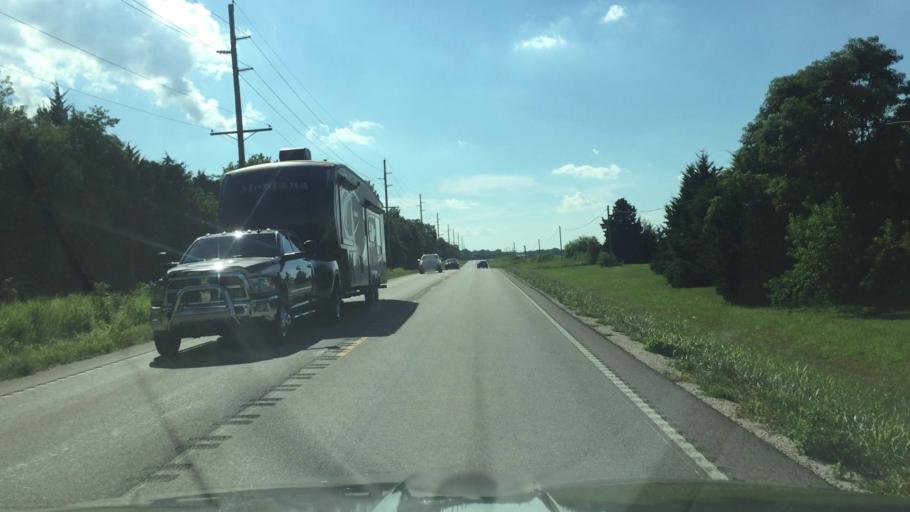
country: US
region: Missouri
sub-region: Morgan County
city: Versailles
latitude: 38.4014
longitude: -92.7445
